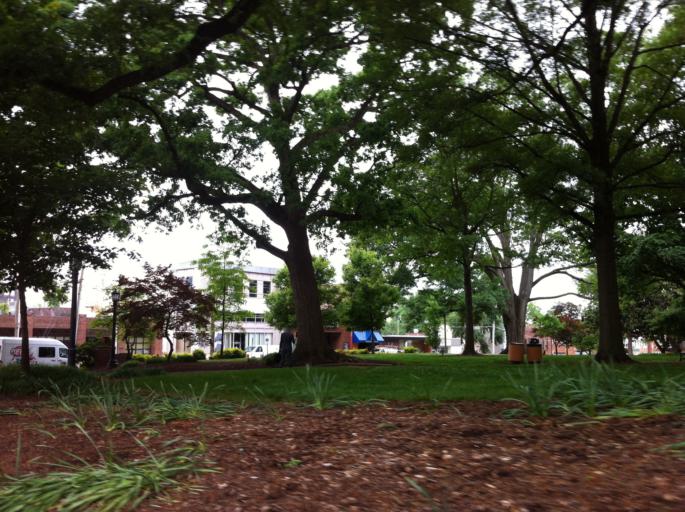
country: US
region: North Carolina
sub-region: Wake County
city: Raleigh
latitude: 35.7775
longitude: -78.6420
